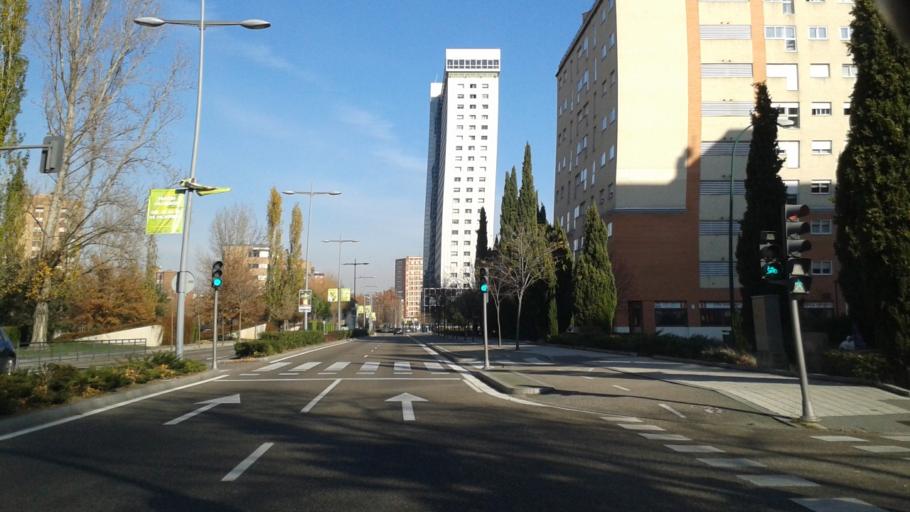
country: ES
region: Castille and Leon
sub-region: Provincia de Valladolid
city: Valladolid
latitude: 41.6568
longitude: -4.7357
